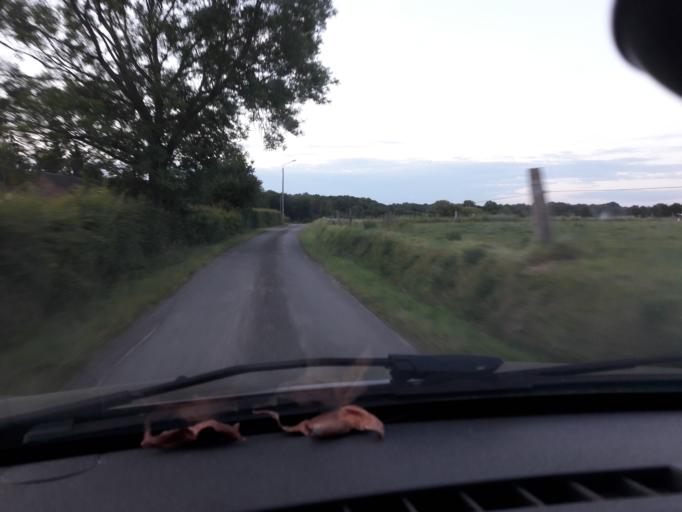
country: BE
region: Wallonia
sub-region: Province du Hainaut
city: Beaumont
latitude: 50.2658
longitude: 4.1880
